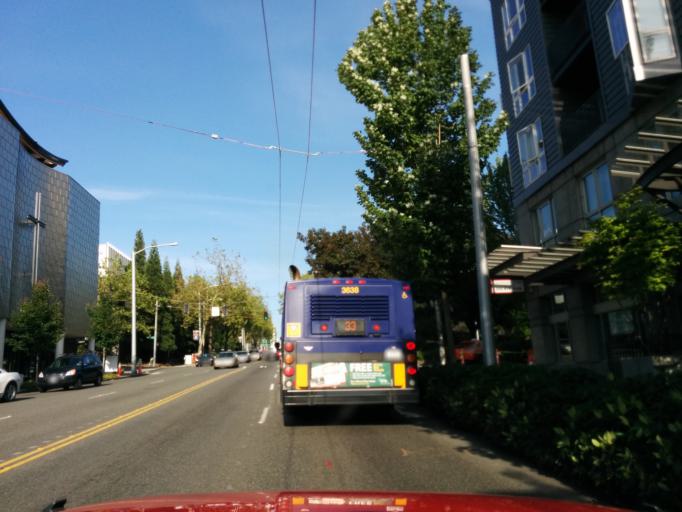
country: US
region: Washington
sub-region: King County
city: Seattle
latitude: 47.6186
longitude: -122.3538
